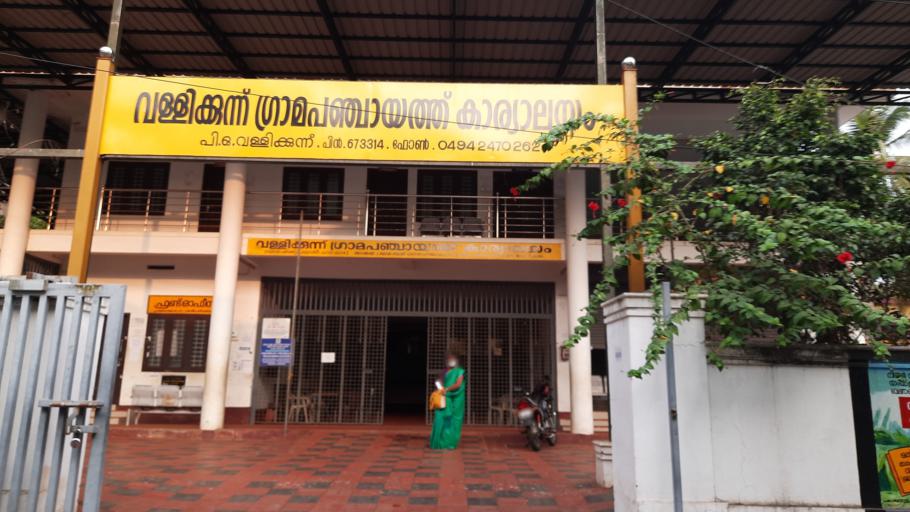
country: IN
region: Kerala
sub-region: Kozhikode
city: Ferokh
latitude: 11.1205
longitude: 75.8464
